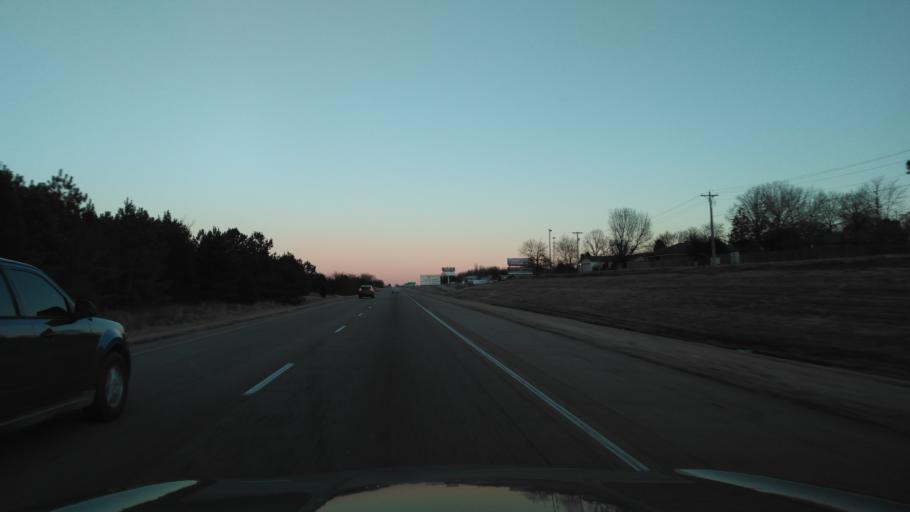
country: US
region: Arkansas
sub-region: Crawford County
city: Van Buren
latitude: 35.4647
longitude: -94.3721
